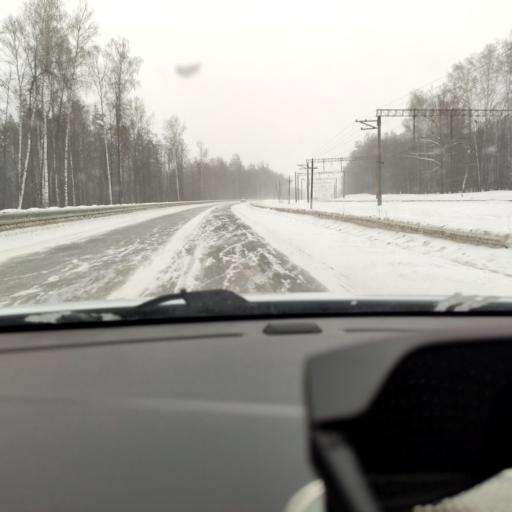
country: RU
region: Tatarstan
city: Vysokaya Gora
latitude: 55.9224
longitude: 49.2854
